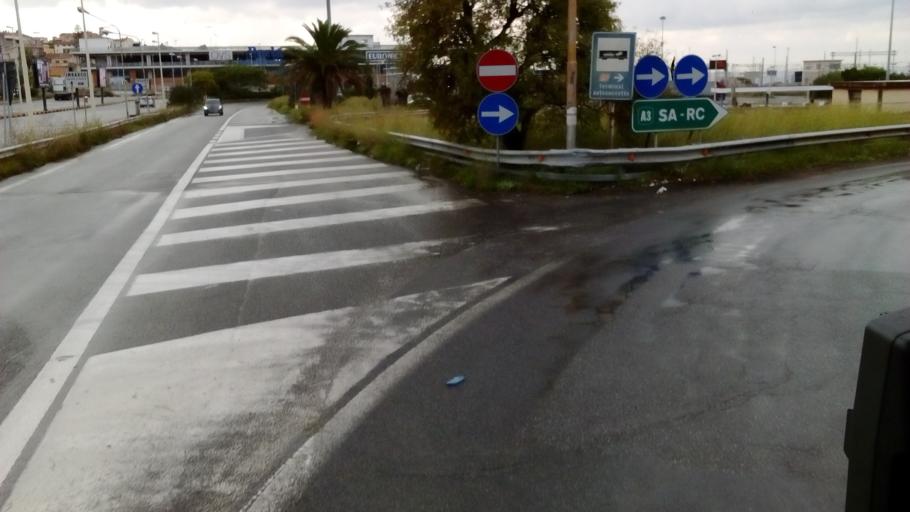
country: IT
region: Calabria
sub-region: Provincia di Reggio Calabria
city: Campo Calabro
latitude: 38.2165
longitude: 15.6363
